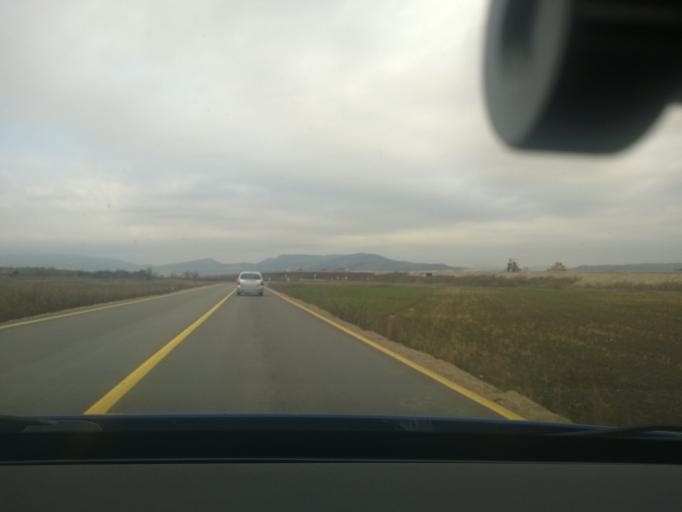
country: RS
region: Central Serbia
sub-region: Pirotski Okrug
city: Pirot
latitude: 43.1168
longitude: 22.6249
